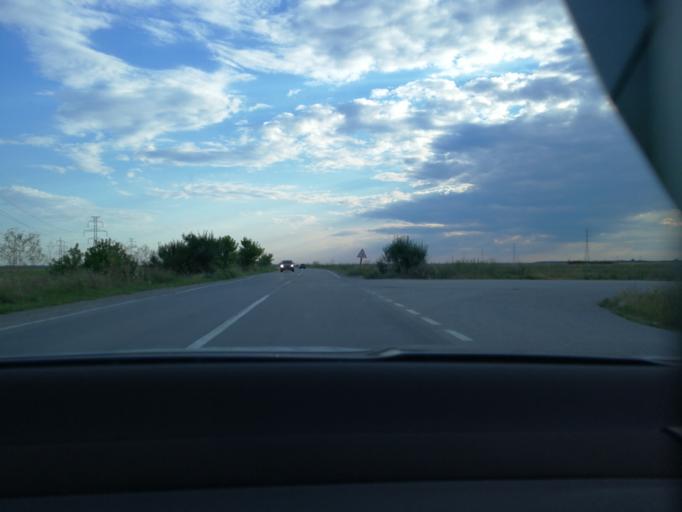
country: RO
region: Prahova
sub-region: Comuna Targsoru Vechi
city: Strejnicu
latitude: 44.8948
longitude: 25.9652
